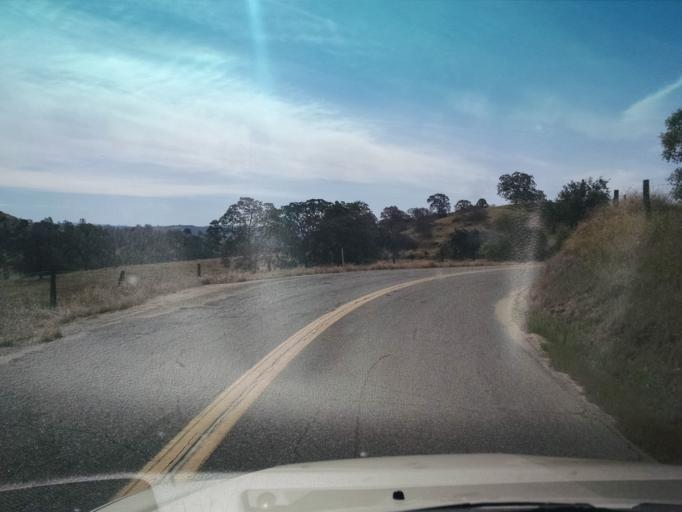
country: US
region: California
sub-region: Madera County
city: Yosemite Lakes
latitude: 37.1158
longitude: -119.6959
